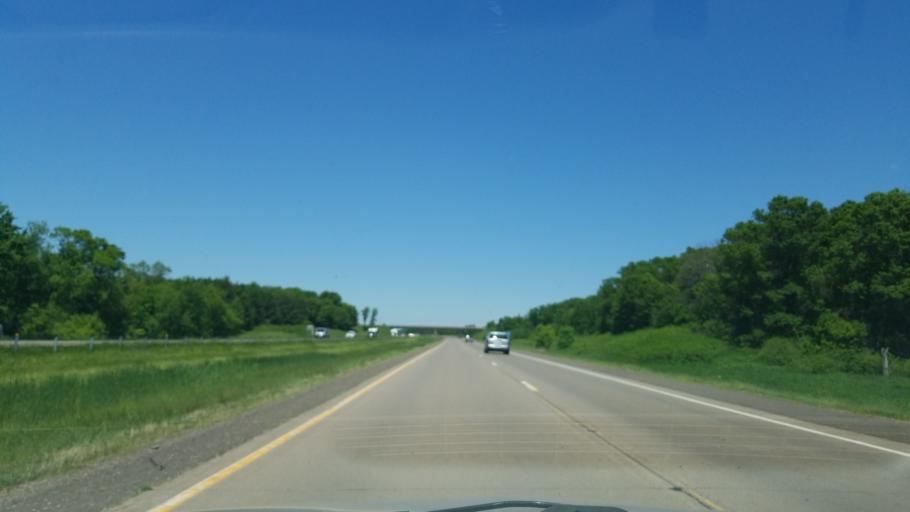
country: US
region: Minnesota
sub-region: Chisago County
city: Harris
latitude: 45.6110
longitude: -92.9930
